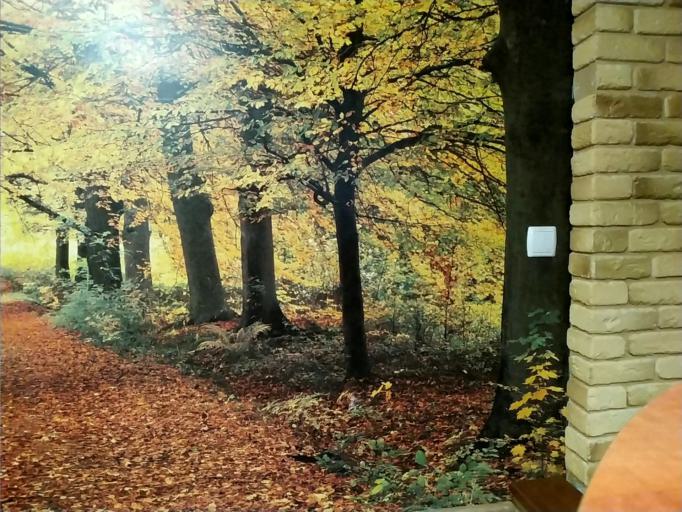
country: BY
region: Minsk
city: Il'ya
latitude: 54.4257
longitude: 27.5623
